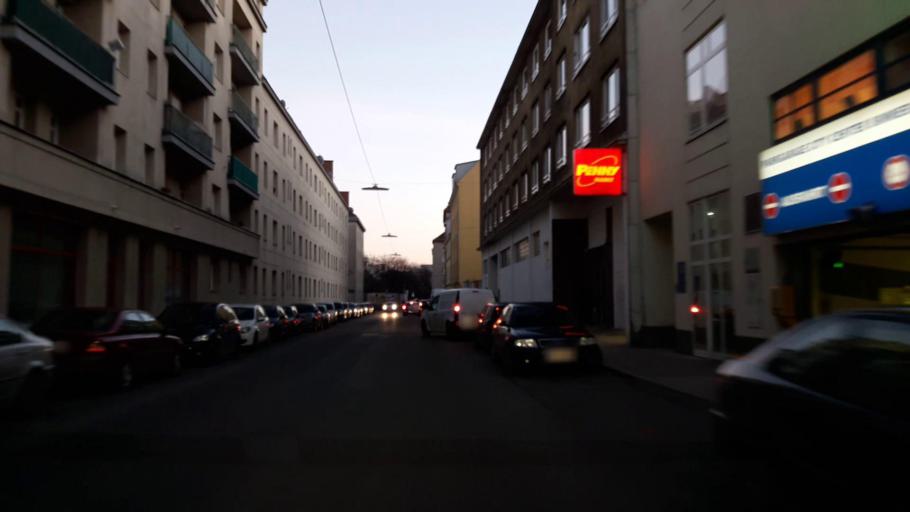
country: AT
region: Vienna
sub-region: Wien Stadt
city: Vienna
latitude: 48.1791
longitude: 16.4120
